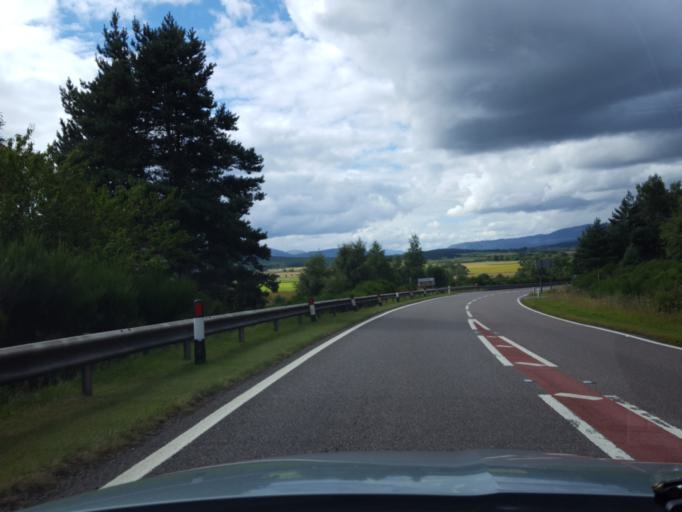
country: GB
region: Scotland
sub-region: Highland
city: Grantown on Spey
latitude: 57.2825
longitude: -3.6703
